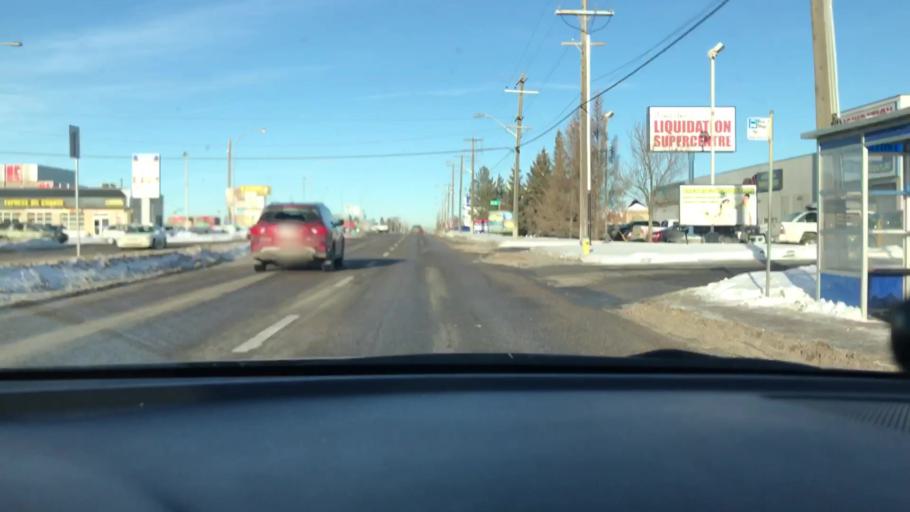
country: CA
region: Alberta
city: Edmonton
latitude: 53.4682
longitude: -113.4860
